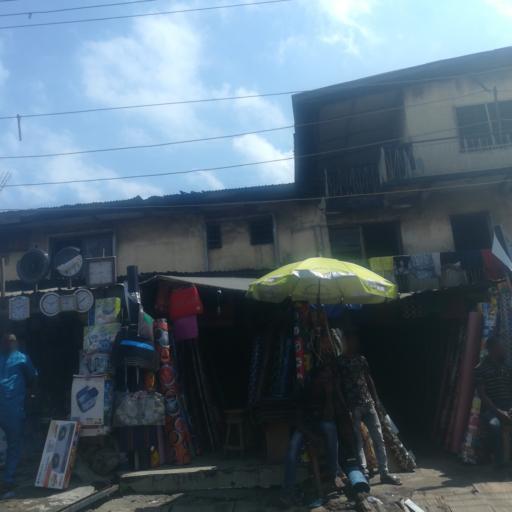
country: NG
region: Lagos
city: Ojota
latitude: 6.5982
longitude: 3.3874
